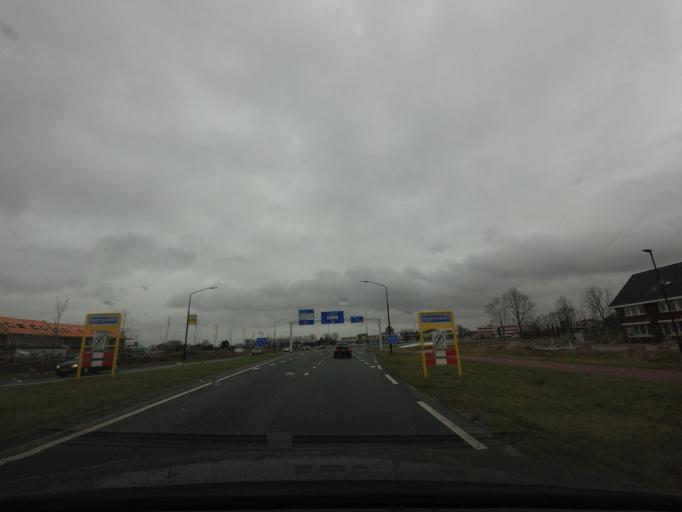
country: NL
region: North Holland
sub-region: Gemeente Langedijk
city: Broek op Langedijk
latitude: 52.6707
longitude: 4.8154
